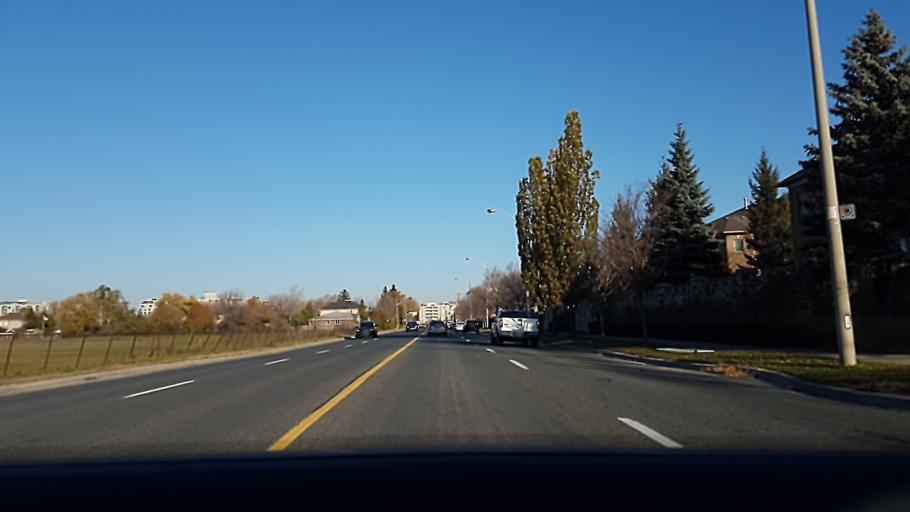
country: CA
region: Ontario
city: North York
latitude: 43.7463
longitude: -79.4539
